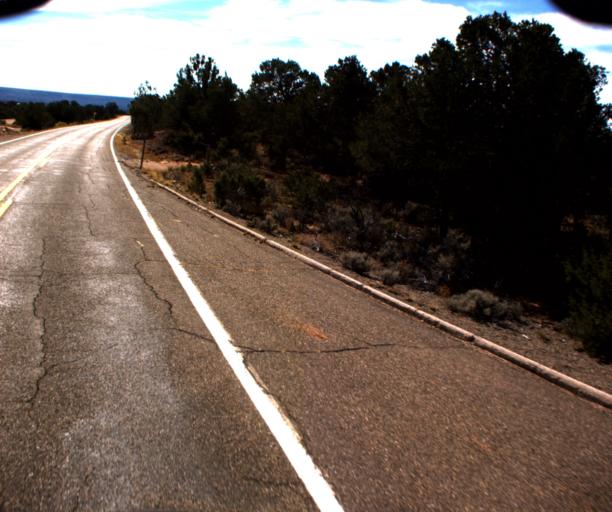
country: US
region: Arizona
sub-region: Navajo County
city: Kayenta
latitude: 36.6374
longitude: -110.5104
